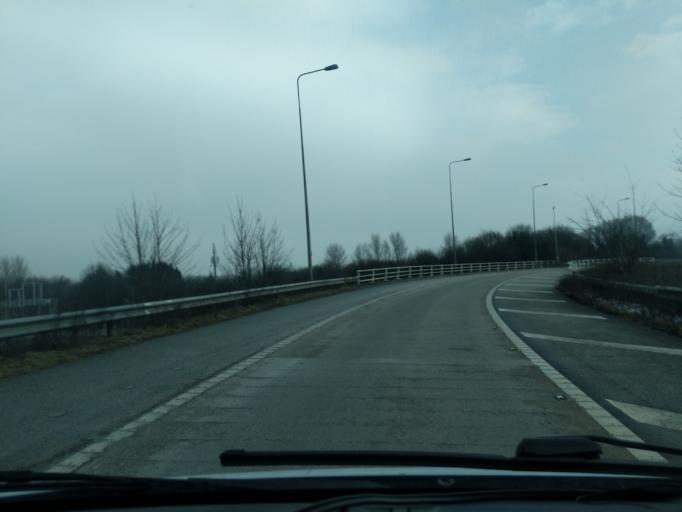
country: GB
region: England
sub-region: Manchester
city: Swinton
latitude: 53.4888
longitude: -2.3784
